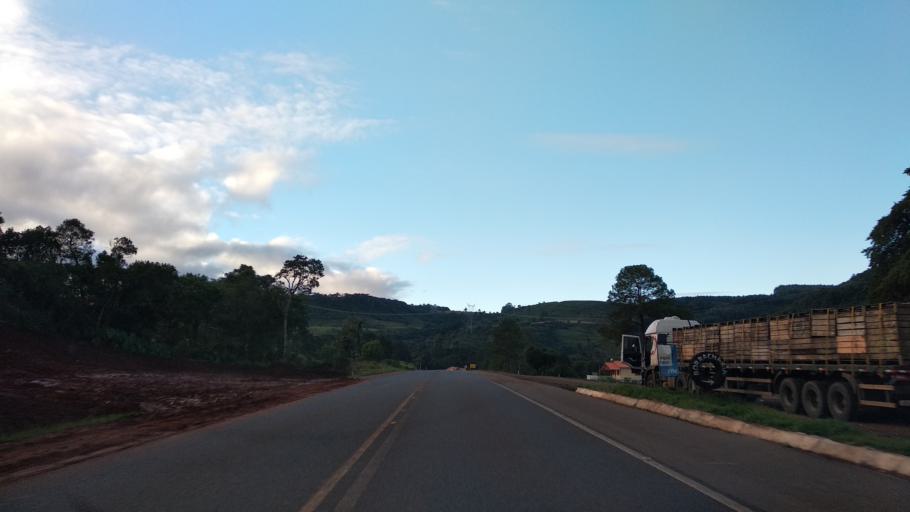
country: BR
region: Santa Catarina
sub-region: Curitibanos
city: Curitibanos
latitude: -27.5577
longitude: -50.8419
